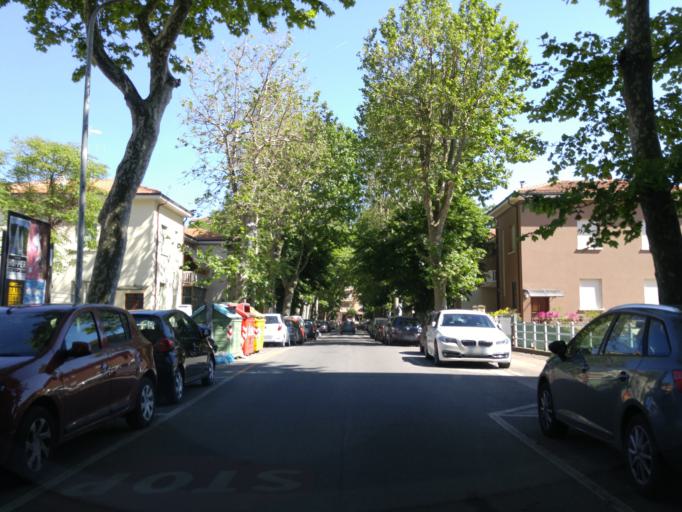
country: IT
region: The Marches
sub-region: Provincia di Pesaro e Urbino
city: Pesaro
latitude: 43.9086
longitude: 12.9220
